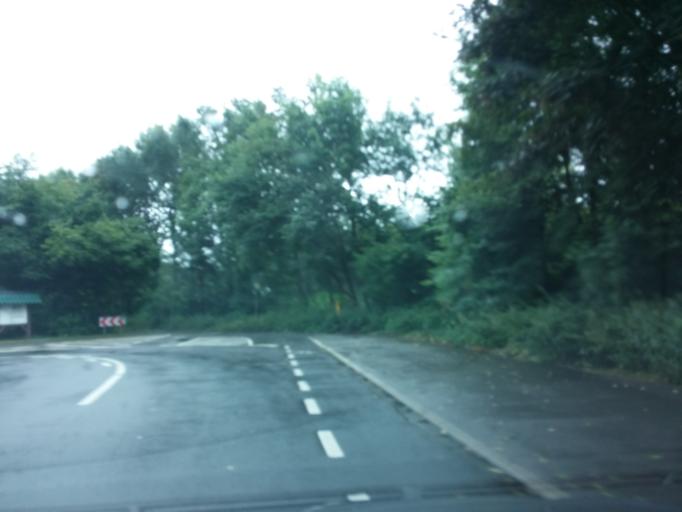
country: DE
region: North Rhine-Westphalia
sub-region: Regierungsbezirk Munster
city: Gladbeck
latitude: 51.5794
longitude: 7.0203
